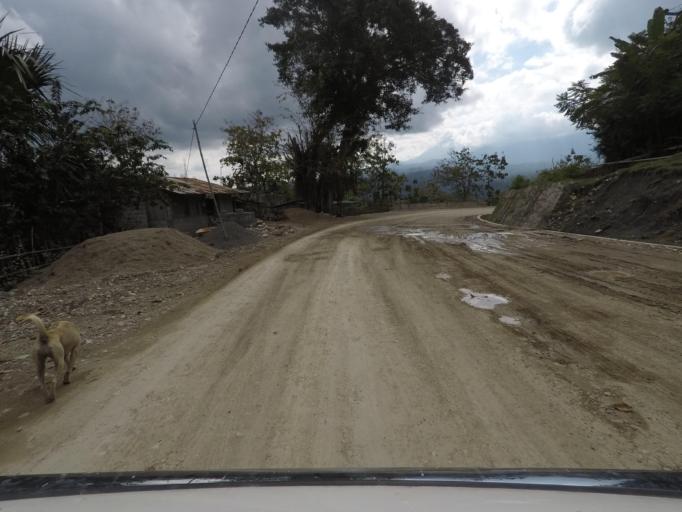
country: TL
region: Viqueque
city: Viqueque
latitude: -8.7894
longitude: 126.3760
